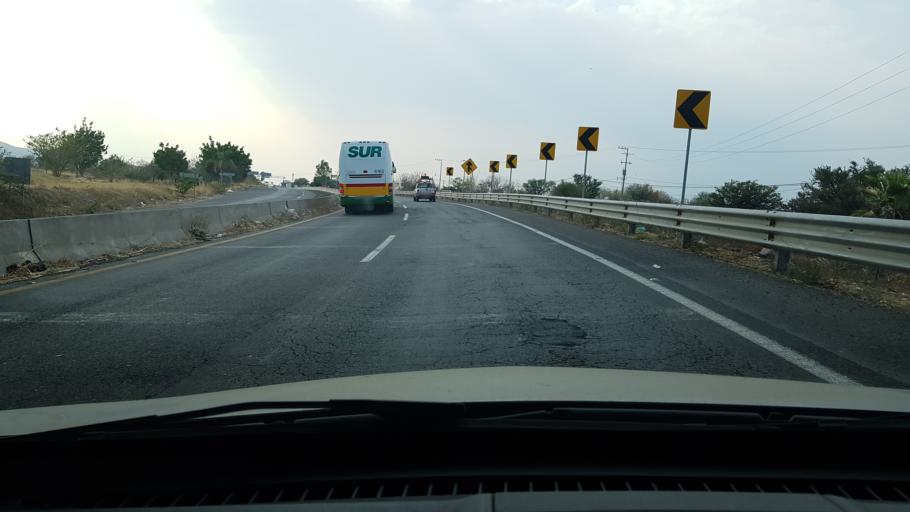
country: MX
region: Morelos
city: Amayuca
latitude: 18.7307
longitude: -98.8116
